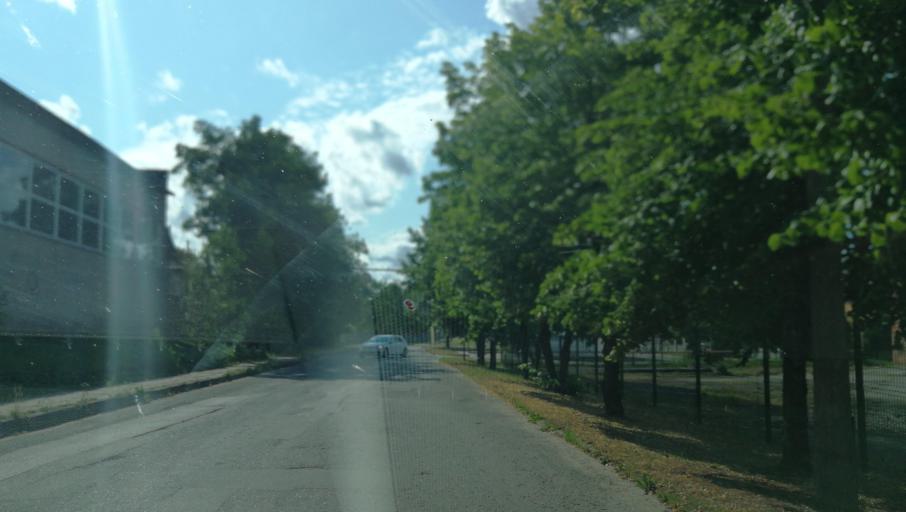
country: LV
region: Cesu Rajons
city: Cesis
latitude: 57.3122
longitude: 25.2886
